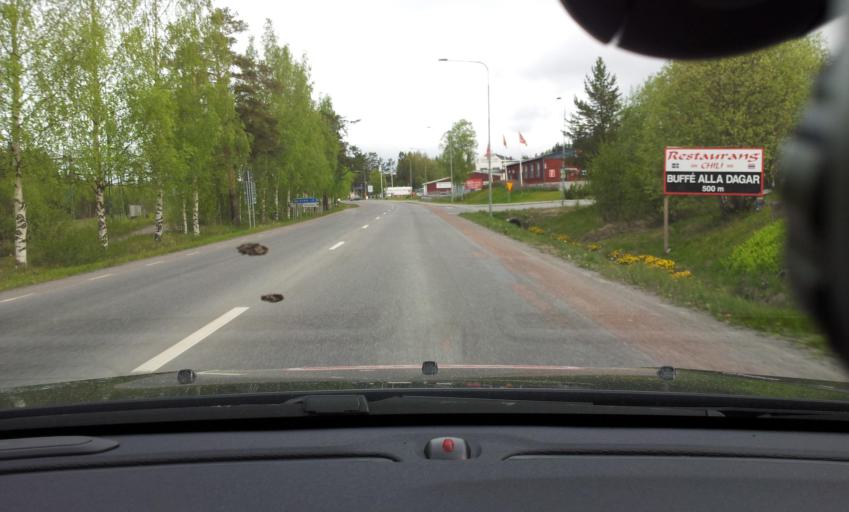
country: SE
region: Jaemtland
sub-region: OEstersunds Kommun
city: Brunflo
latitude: 63.0723
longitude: 14.8401
